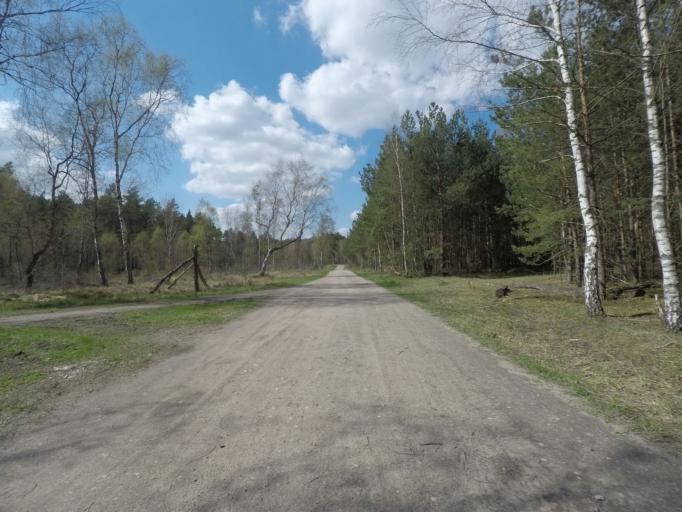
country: DE
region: Brandenburg
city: Marienwerder
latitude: 52.8287
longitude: 13.6602
